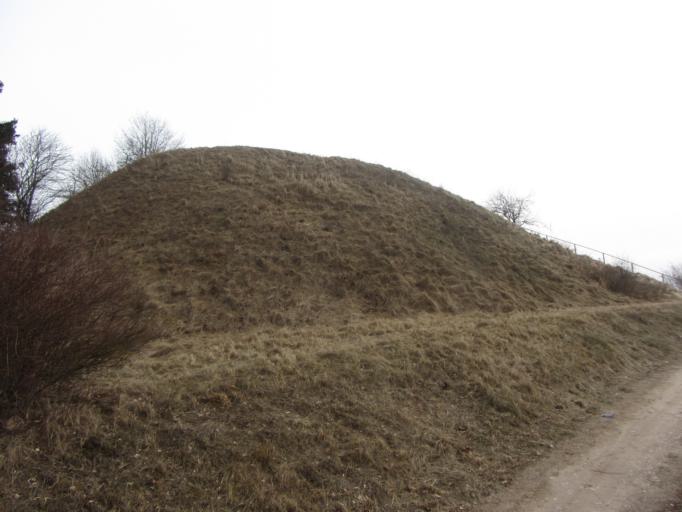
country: LT
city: Prienai
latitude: 54.6240
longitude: 23.7447
